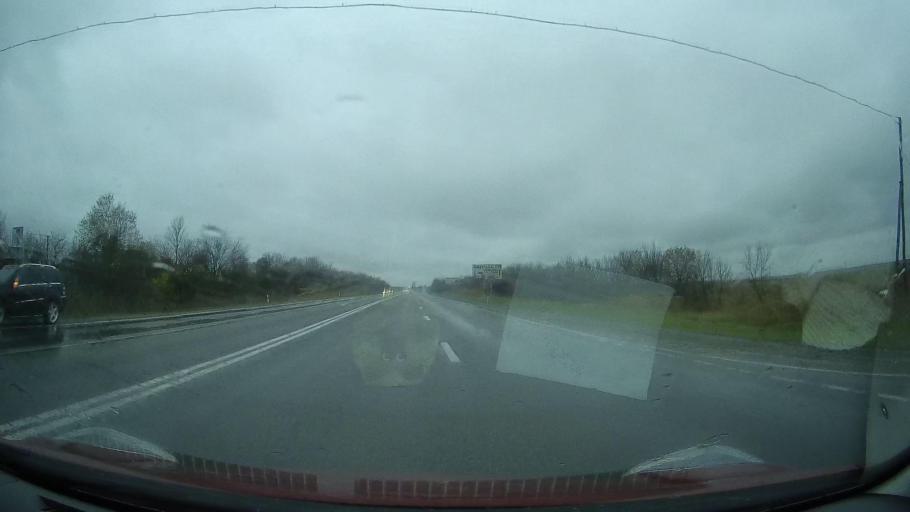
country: RU
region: Stavropol'skiy
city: Nevinnomyssk
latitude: 44.6343
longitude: 42.0063
